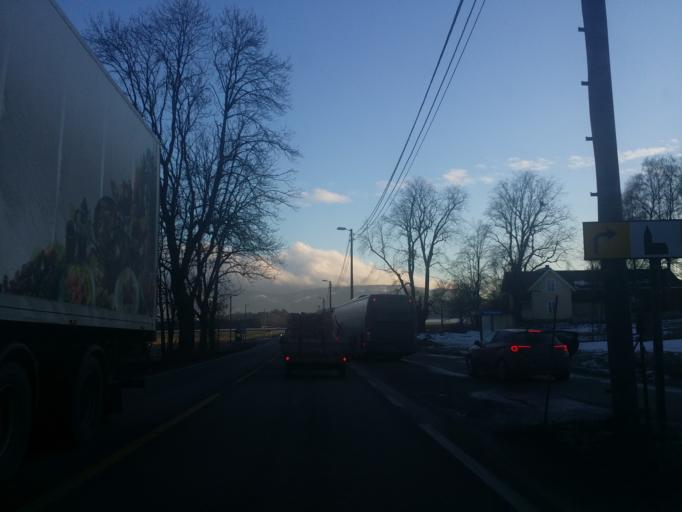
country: NO
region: Buskerud
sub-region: Hole
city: Vik
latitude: 60.1170
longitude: 10.2821
